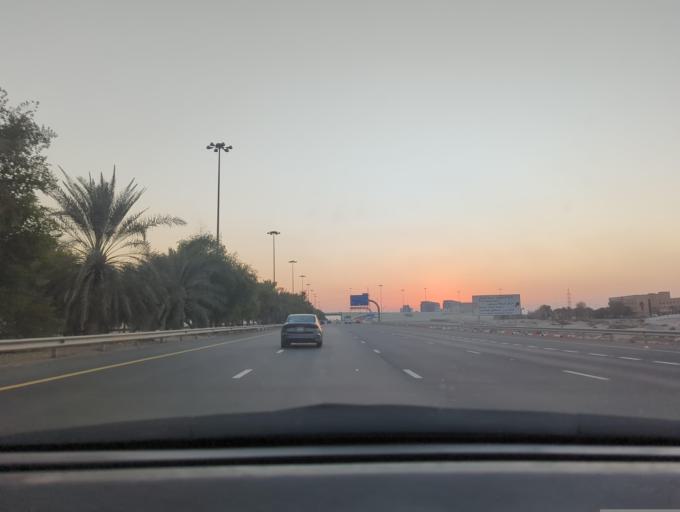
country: AE
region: Abu Dhabi
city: Abu Dhabi
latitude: 24.3310
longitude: 54.6283
